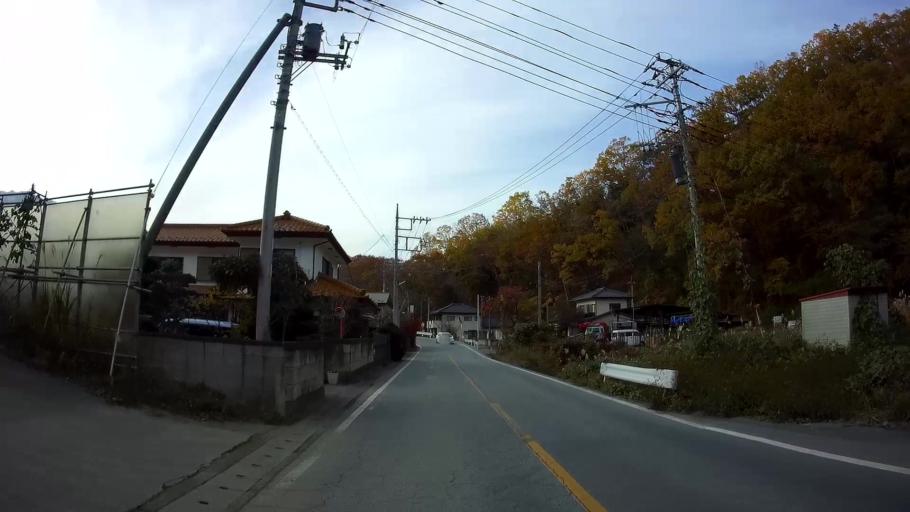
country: JP
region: Yamanashi
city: Ryuo
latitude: 35.4819
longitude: 138.4592
